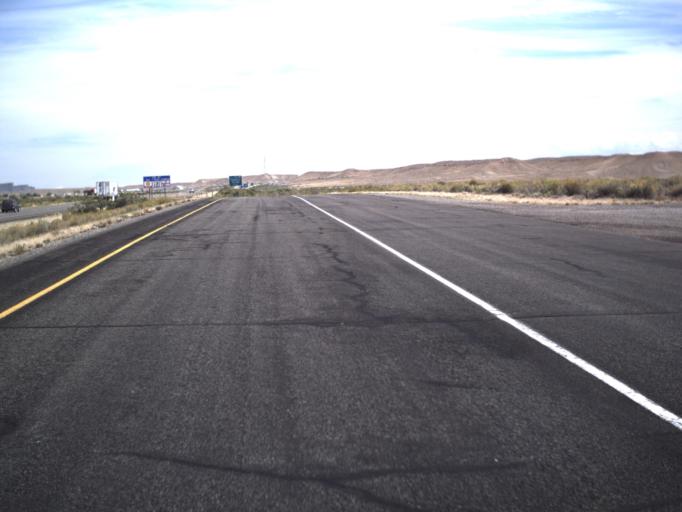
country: US
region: Utah
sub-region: Grand County
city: Moab
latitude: 38.9546
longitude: -109.7530
